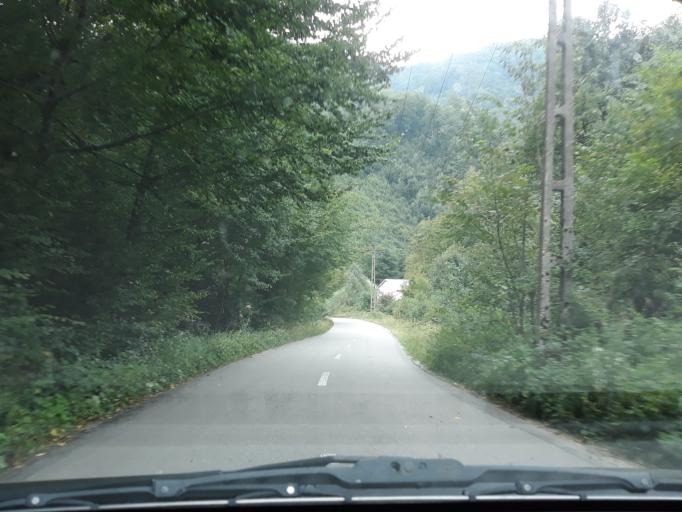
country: RO
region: Bihor
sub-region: Comuna Pietroasa
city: Pietroasa
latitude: 46.5912
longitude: 22.6322
